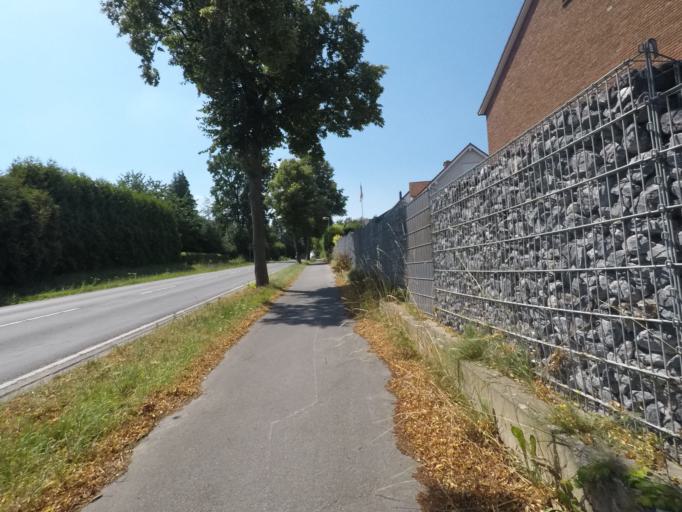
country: DE
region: North Rhine-Westphalia
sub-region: Regierungsbezirk Detmold
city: Hiddenhausen
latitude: 52.1148
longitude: 8.6066
